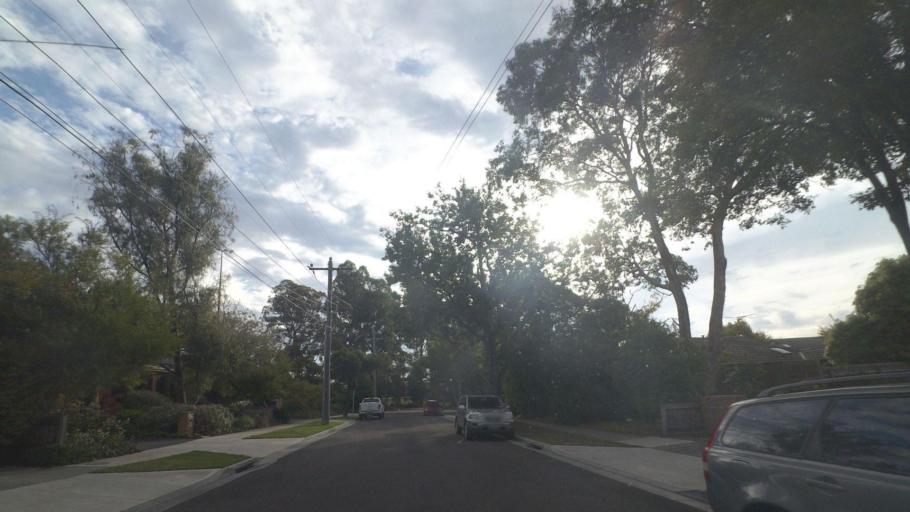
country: AU
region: Victoria
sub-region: Whitehorse
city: Blackburn
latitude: -37.8216
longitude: 145.1581
